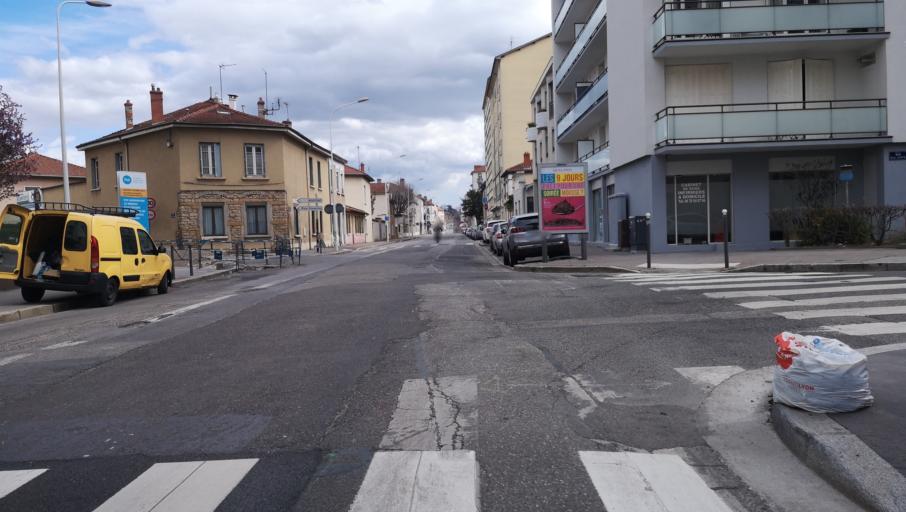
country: FR
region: Rhone-Alpes
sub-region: Departement du Rhone
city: Villeurbanne
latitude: 45.7474
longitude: 4.8823
